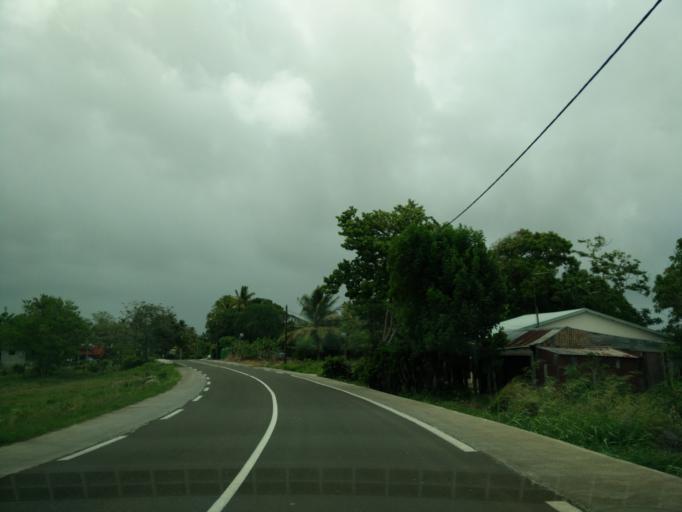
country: GP
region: Guadeloupe
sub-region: Guadeloupe
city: Grand-Bourg
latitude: 15.9043
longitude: -61.2570
